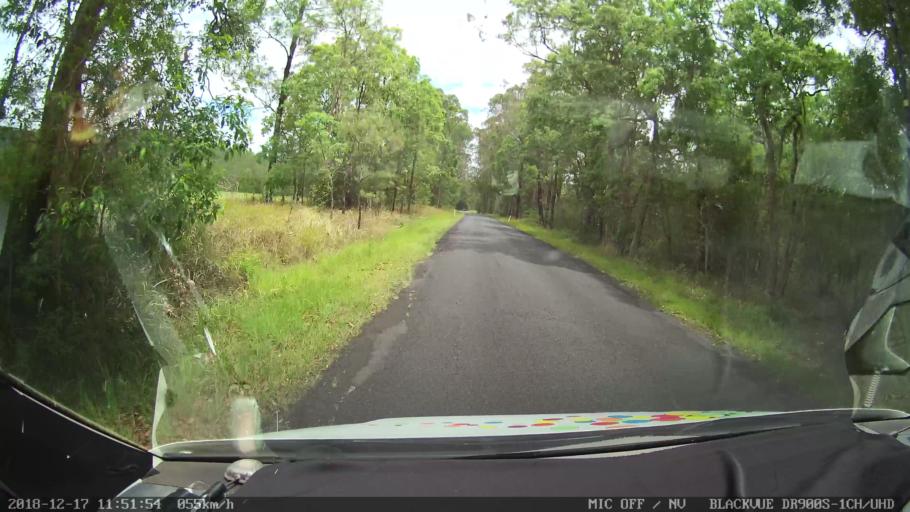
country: AU
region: New South Wales
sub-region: Kyogle
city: Kyogle
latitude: -28.5854
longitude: 152.5910
